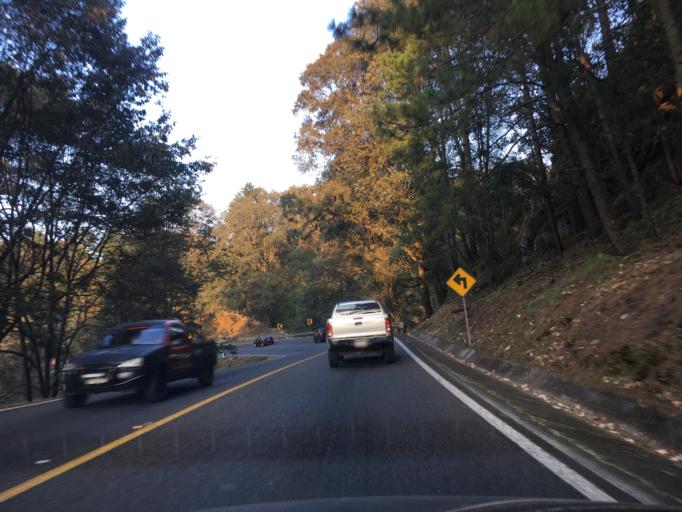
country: MX
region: Michoacan
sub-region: Patzcuaro
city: Santa Maria Huiramangaro (San Juan Tumbio)
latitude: 19.4909
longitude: -101.7168
